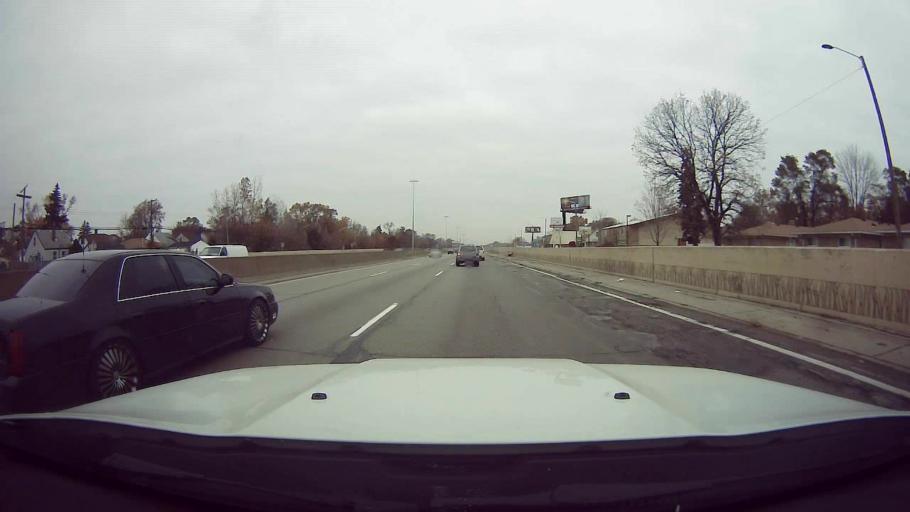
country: US
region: Michigan
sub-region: Wayne County
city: Dearborn
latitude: 42.3468
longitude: -83.2161
